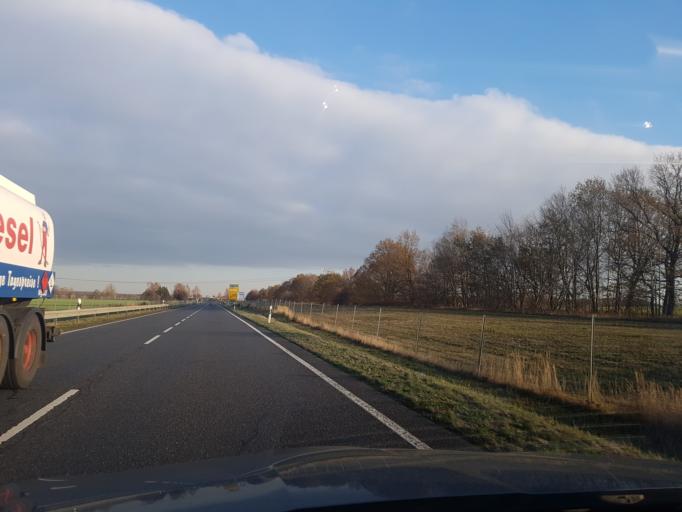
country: DE
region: Brandenburg
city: Luckau
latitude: 51.8469
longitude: 13.6828
